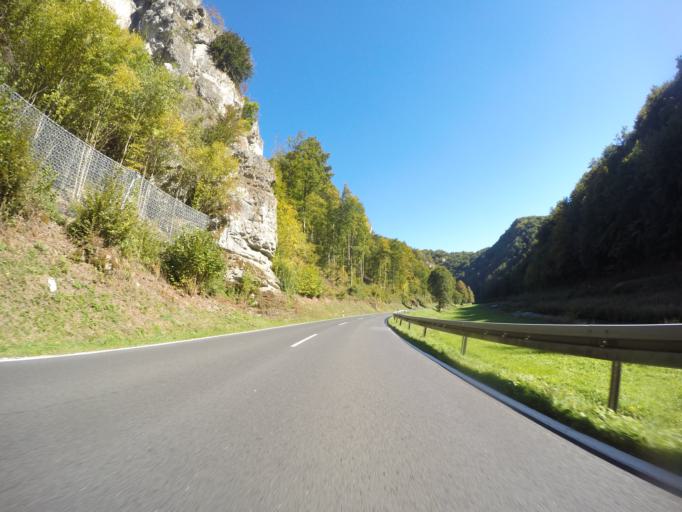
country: DE
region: Bavaria
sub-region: Upper Franconia
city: Gossweinstein
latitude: 49.7716
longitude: 11.3223
